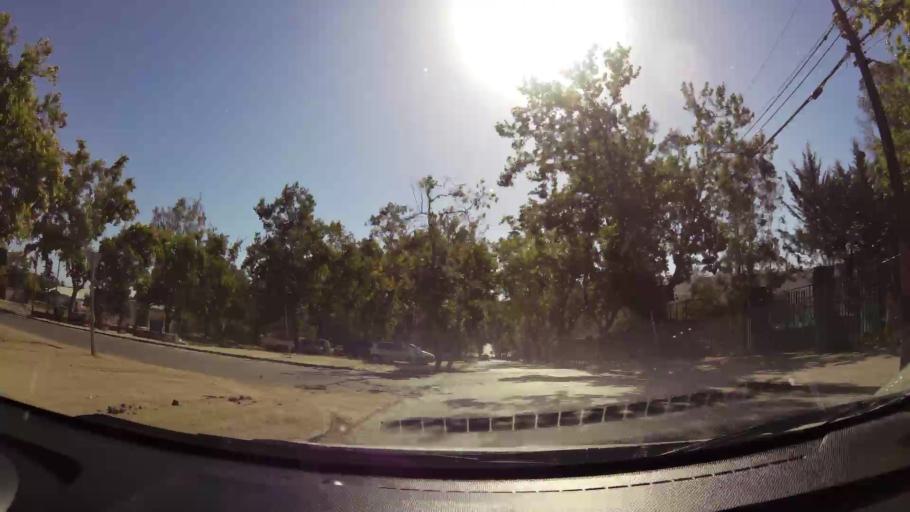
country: CL
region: Maule
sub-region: Provincia de Talca
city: Talca
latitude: -35.4212
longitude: -71.6730
